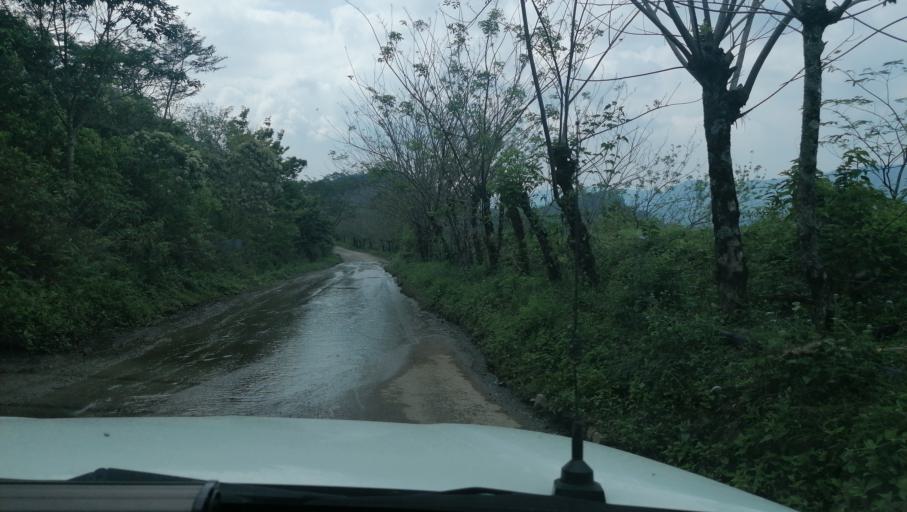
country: MX
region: Chiapas
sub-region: Francisco Leon
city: San Miguel la Sardina
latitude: 17.2369
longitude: -93.3086
